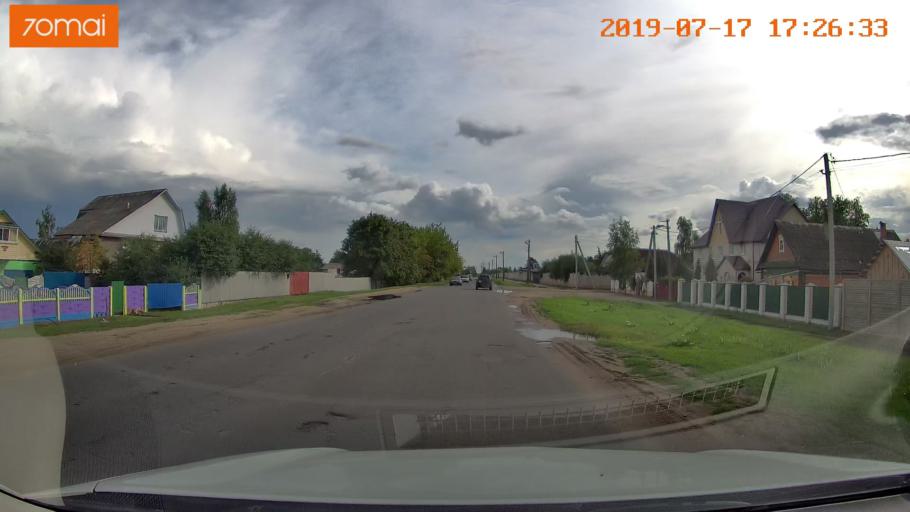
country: BY
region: Mogilev
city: Babruysk
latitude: 53.1407
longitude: 29.1717
